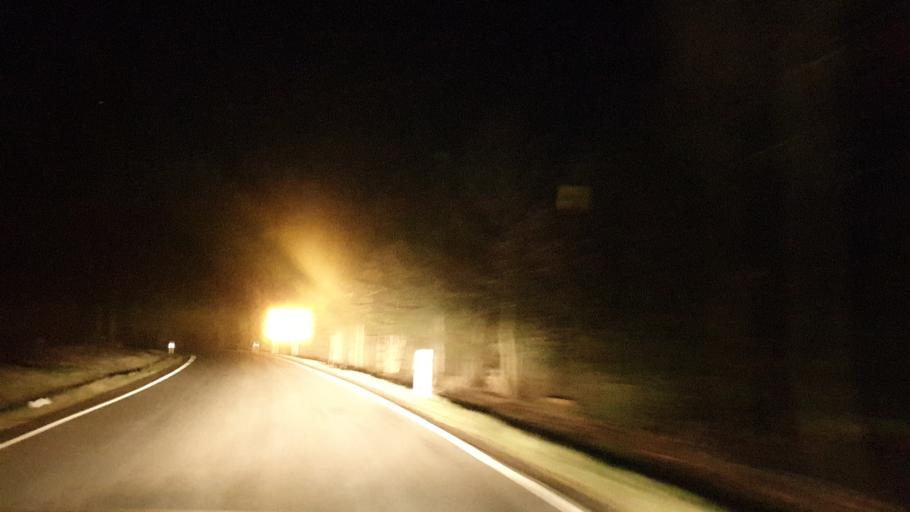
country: DE
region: Rheinland-Pfalz
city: Oberdreis
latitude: 50.6343
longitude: 7.6521
